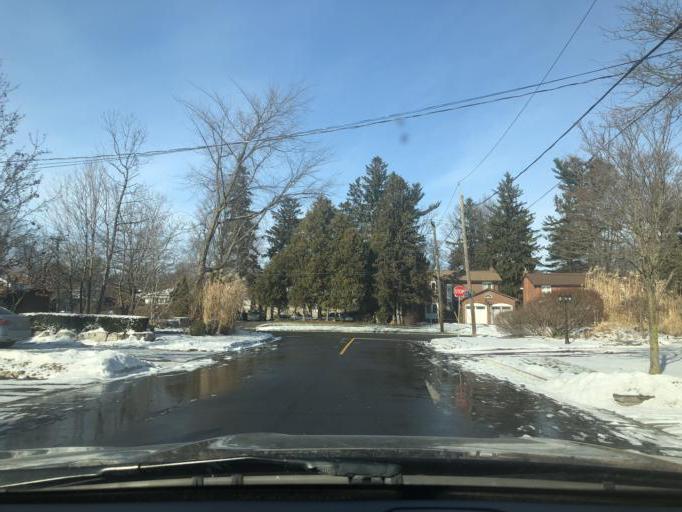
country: CA
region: Ontario
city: Scarborough
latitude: 43.7861
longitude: -79.1550
